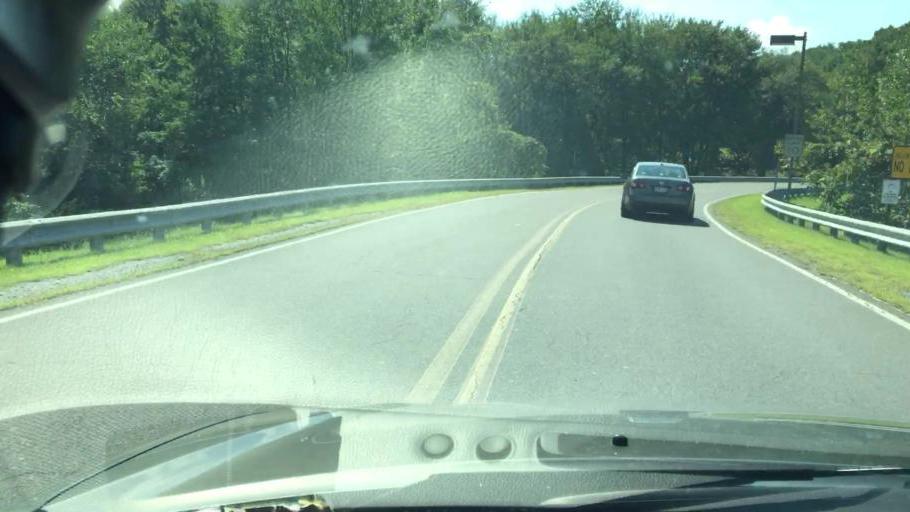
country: US
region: Pennsylvania
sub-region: Luzerne County
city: Nanticoke
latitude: 41.1932
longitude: -75.9882
